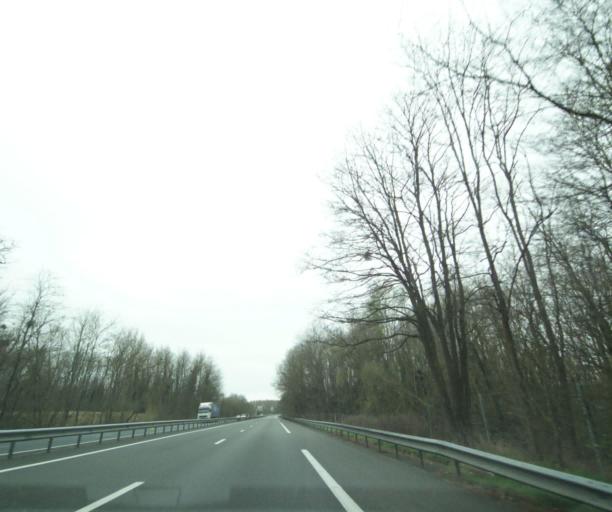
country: FR
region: Centre
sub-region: Departement du Cher
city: Mereau
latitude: 47.2057
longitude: 2.0363
